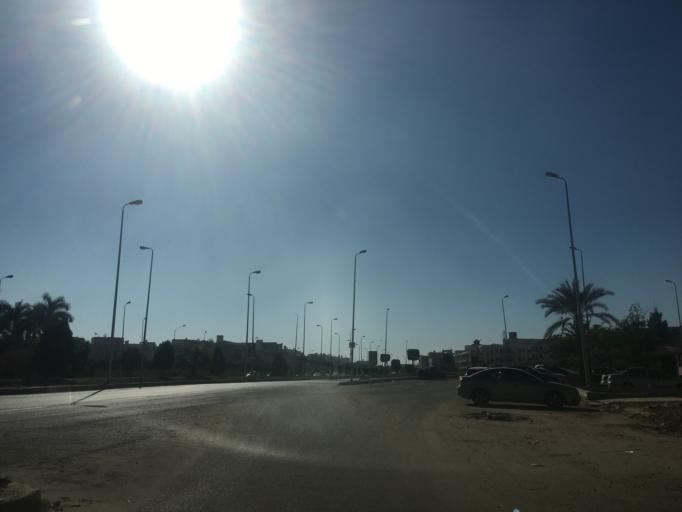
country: EG
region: Al Jizah
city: Awsim
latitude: 30.0249
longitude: 30.9851
